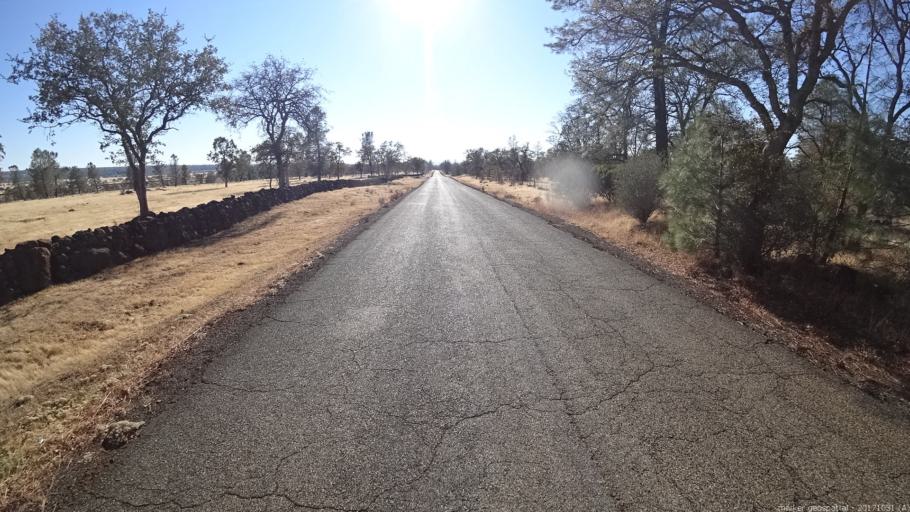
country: US
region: California
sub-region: Shasta County
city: Palo Cedro
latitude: 40.4689
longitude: -122.0933
